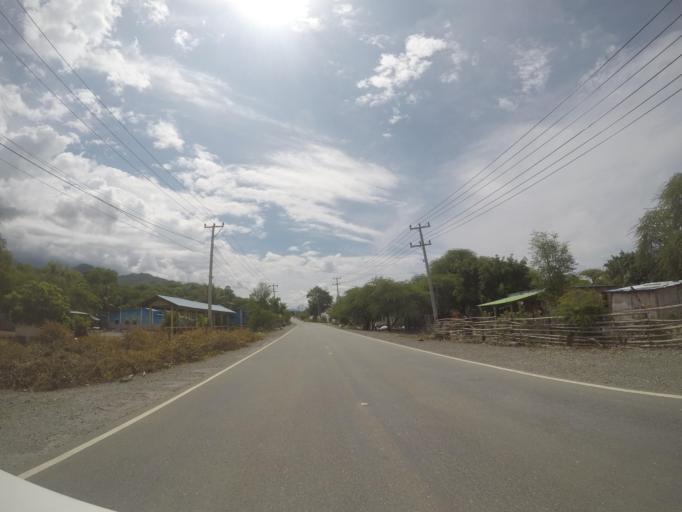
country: TL
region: Liquica
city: Liquica
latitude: -8.5670
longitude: 125.3877
